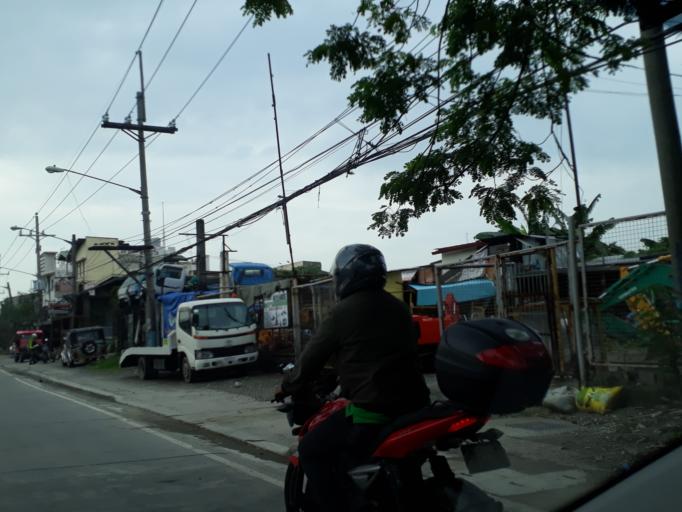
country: PH
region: Calabarzon
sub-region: Province of Rizal
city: Valenzuela
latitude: 14.7150
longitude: 120.9580
